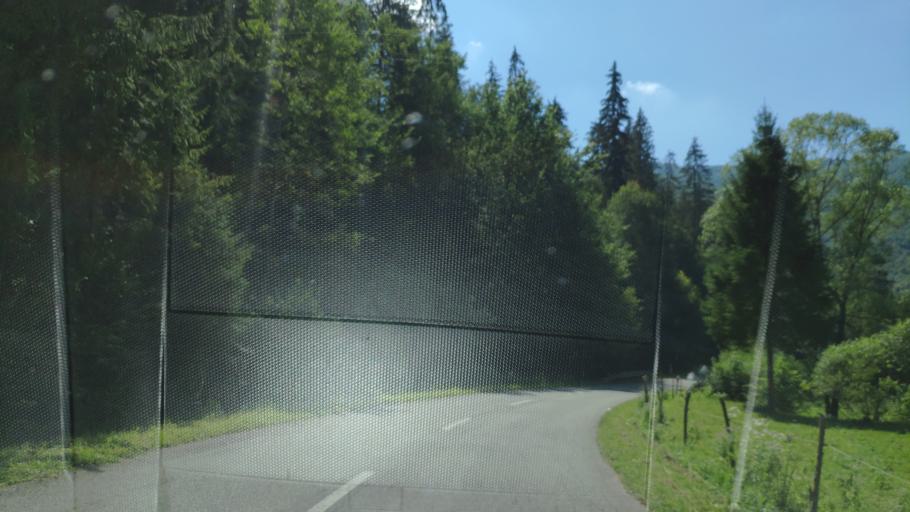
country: PL
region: Subcarpathian Voivodeship
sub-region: Powiat leski
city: Cisna
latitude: 49.0673
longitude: 22.3977
